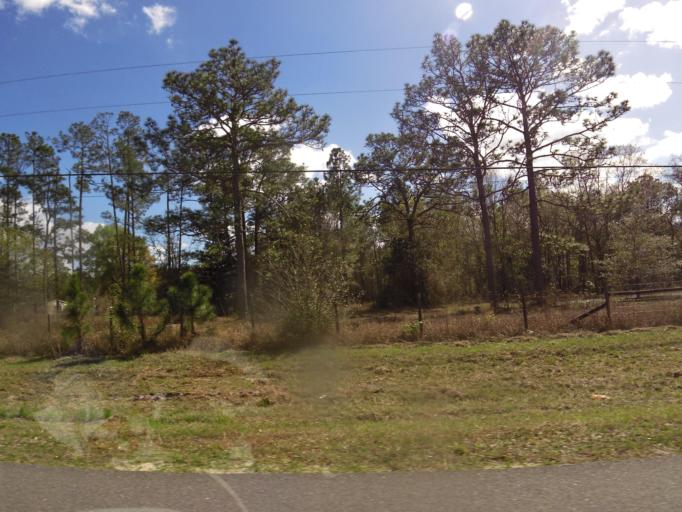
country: US
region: Florida
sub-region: Clay County
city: Middleburg
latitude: 30.1150
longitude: -81.9598
